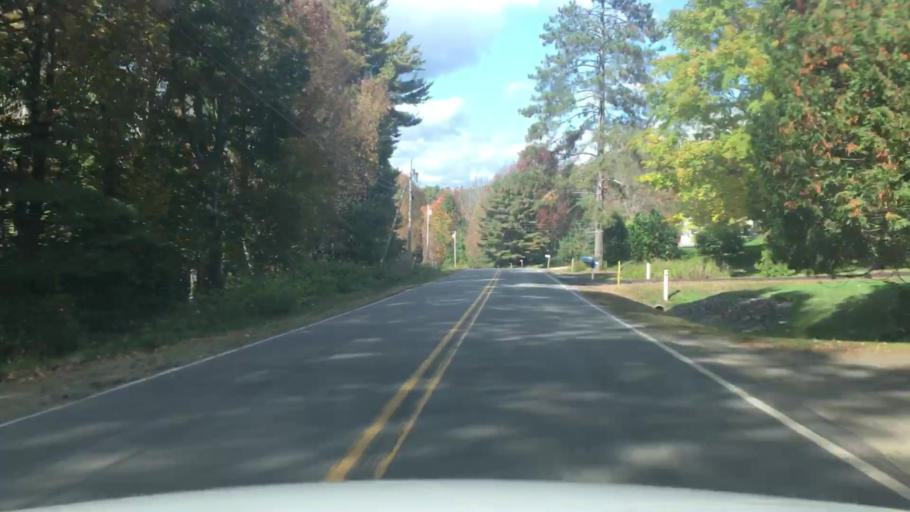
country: US
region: Maine
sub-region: Knox County
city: Warren
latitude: 44.1618
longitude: -69.2441
